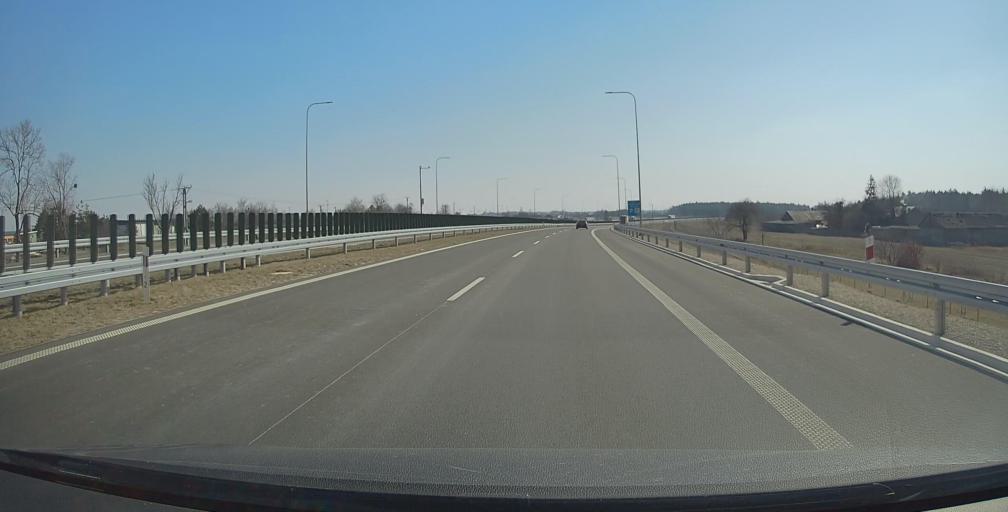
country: PL
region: Lublin Voivodeship
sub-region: Powiat janowski
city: Janow Lubelski
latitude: 50.7213
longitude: 22.3755
